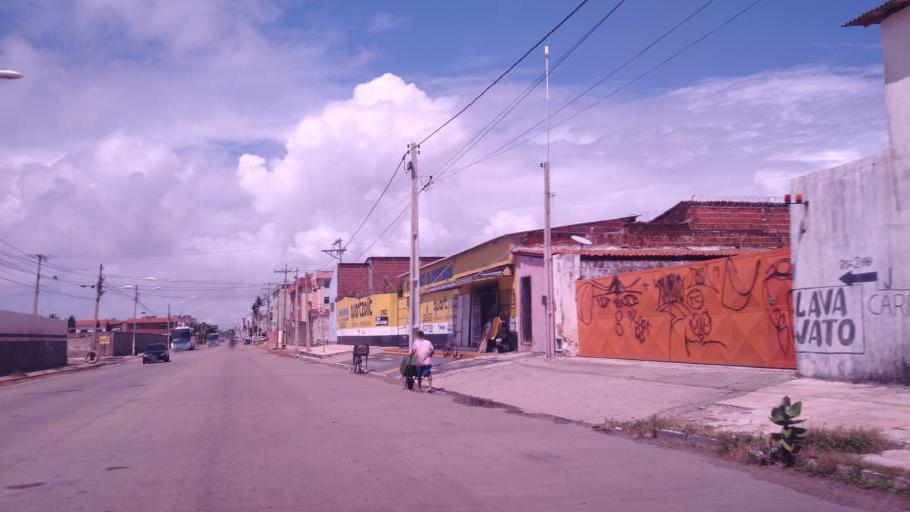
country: BR
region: Ceara
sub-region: Fortaleza
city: Fortaleza
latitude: -3.7201
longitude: -38.4649
